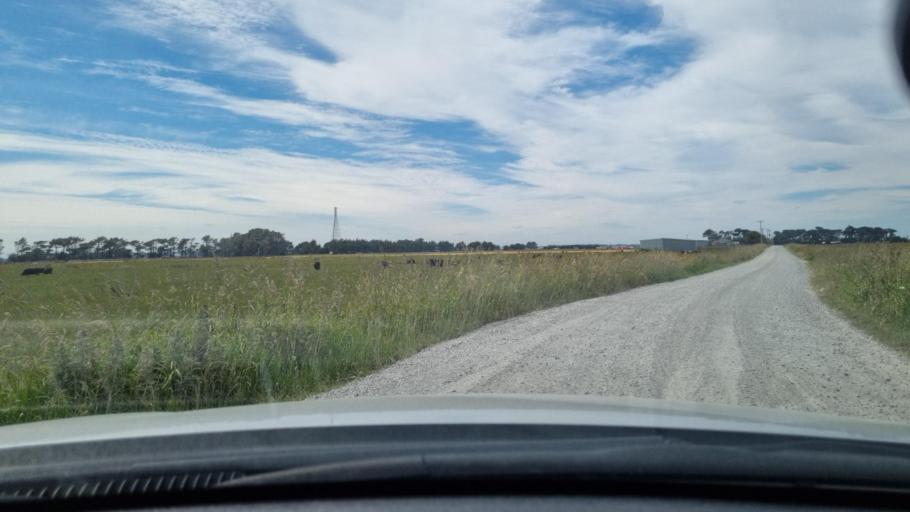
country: NZ
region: Southland
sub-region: Invercargill City
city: Invercargill
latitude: -46.4011
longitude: 168.2838
